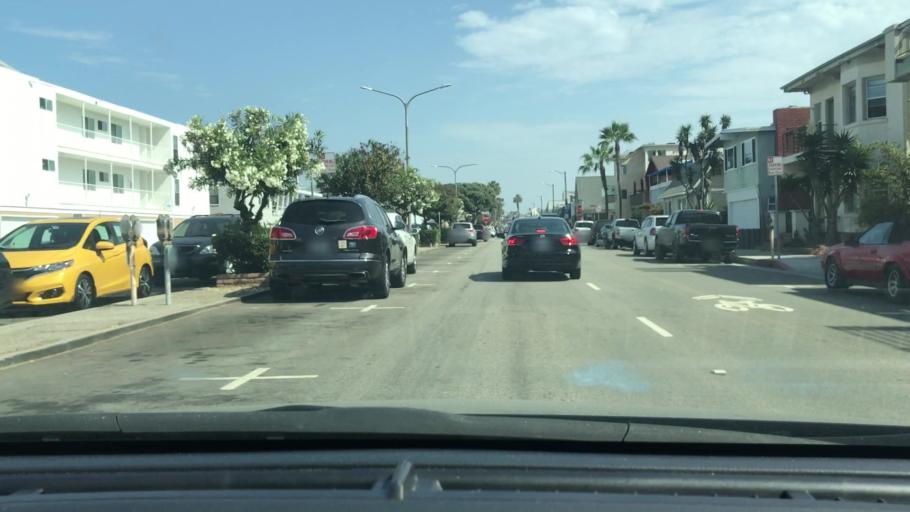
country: US
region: California
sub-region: Los Angeles County
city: Hermosa Beach
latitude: 33.8584
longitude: -118.3990
